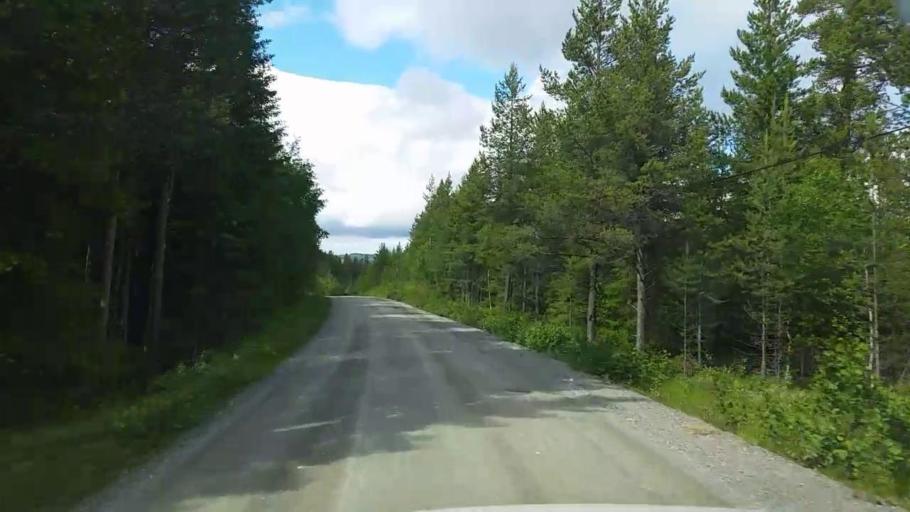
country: NO
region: Hedmark
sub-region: Engerdal
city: Engerdal
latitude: 62.4184
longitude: 12.6781
